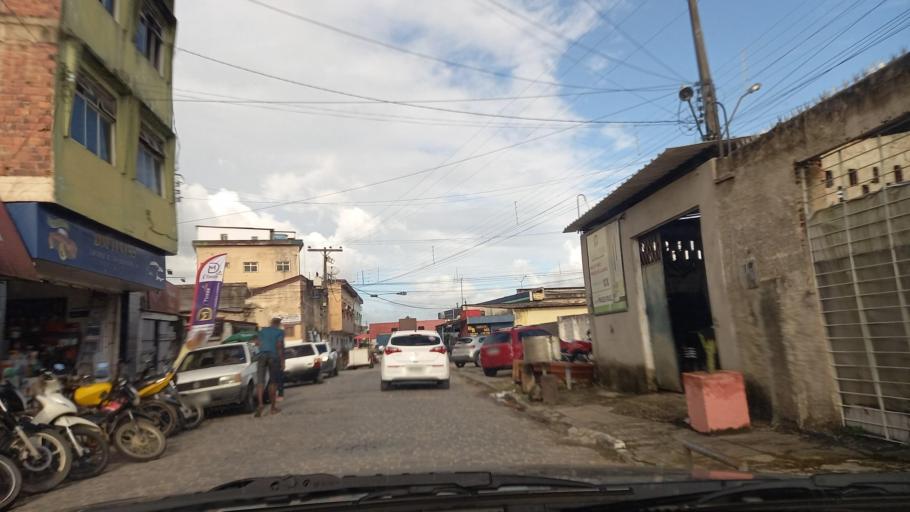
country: BR
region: Pernambuco
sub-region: Palmares
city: Palmares
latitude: -8.6761
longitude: -35.5781
